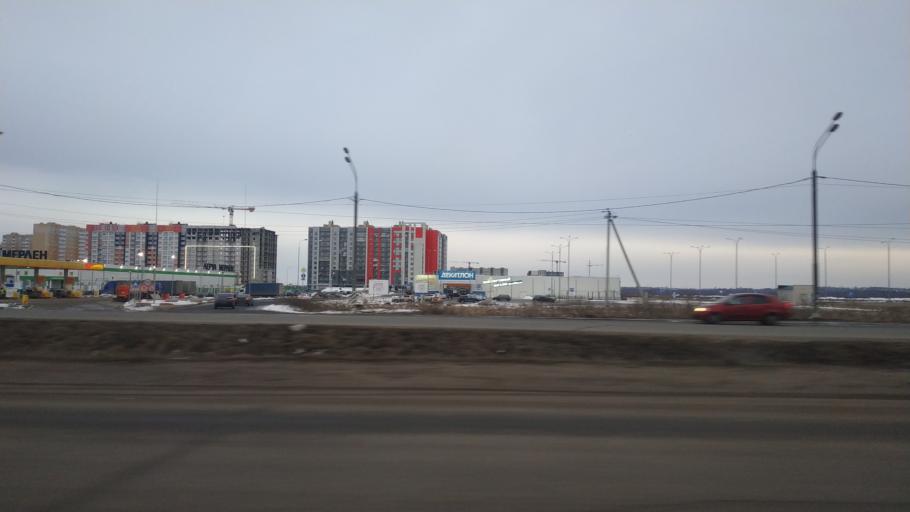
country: RU
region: Tverskaya
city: Tver
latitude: 56.8134
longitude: 35.8778
